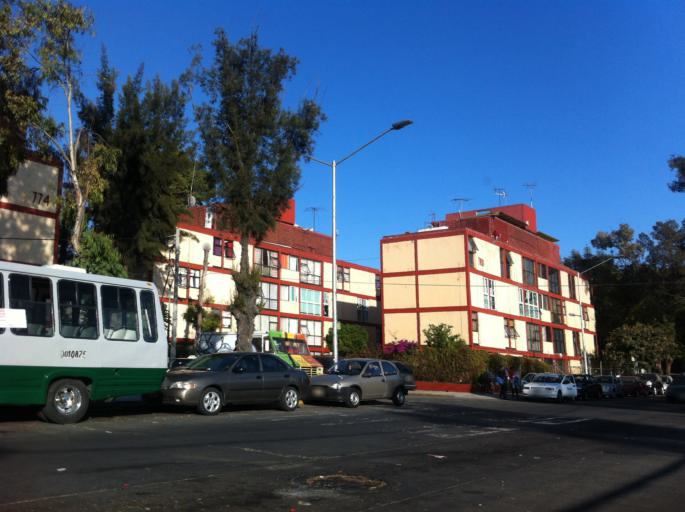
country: MX
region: Mexico City
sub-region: Iztacalco
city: Iztacalco
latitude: 19.4106
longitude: -99.0993
